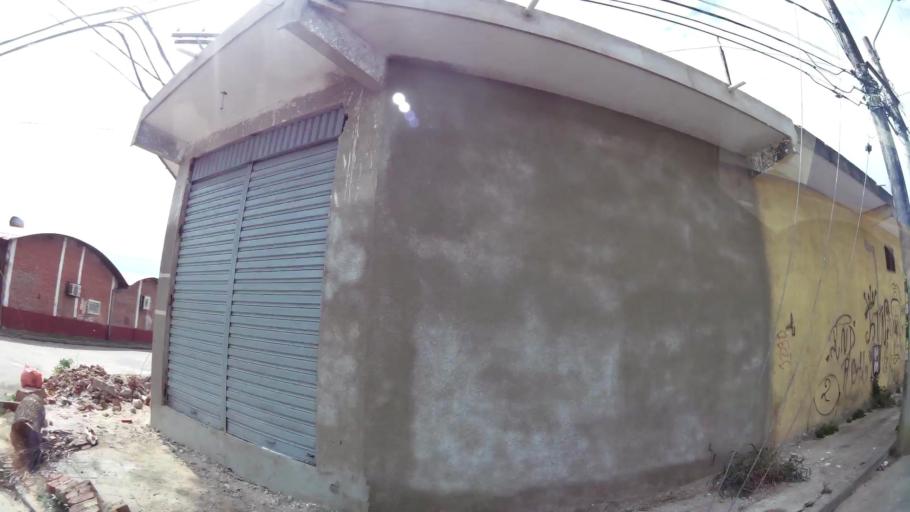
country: BO
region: Santa Cruz
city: Santa Cruz de la Sierra
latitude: -17.7815
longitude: -63.2070
